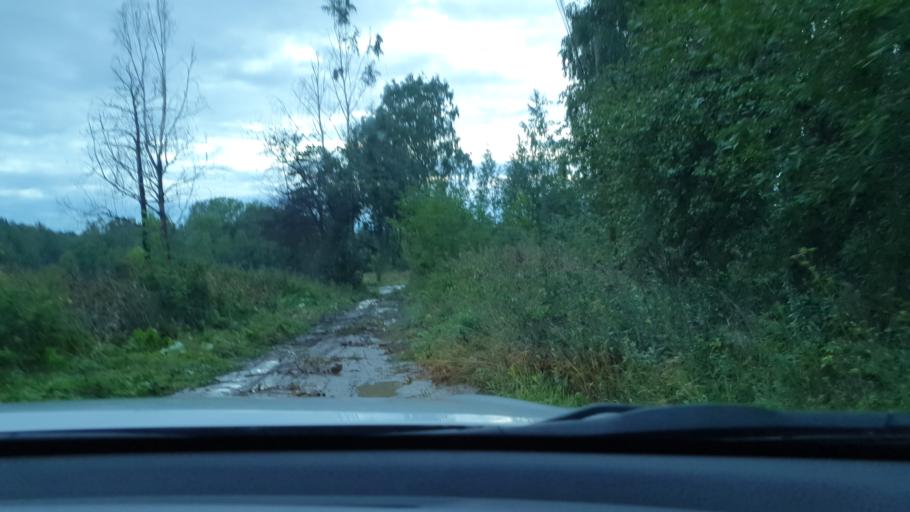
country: RU
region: Sverdlovsk
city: Istok
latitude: 56.7666
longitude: 60.7058
